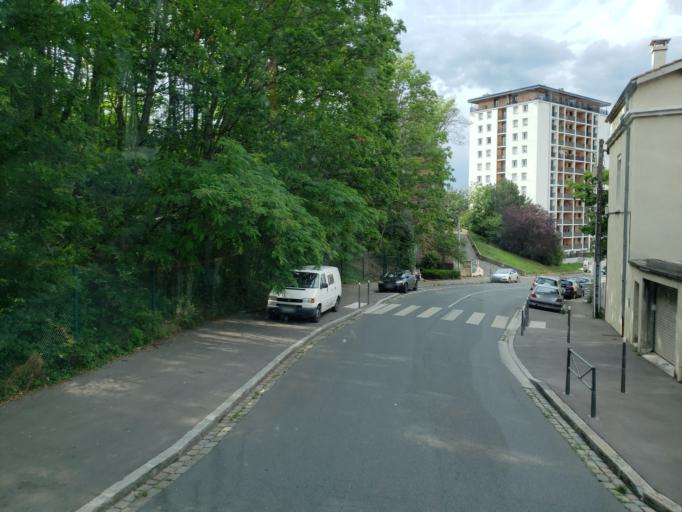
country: FR
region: Rhone-Alpes
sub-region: Departement du Rhone
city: Tassin-la-Demi-Lune
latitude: 45.7666
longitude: 4.8095
